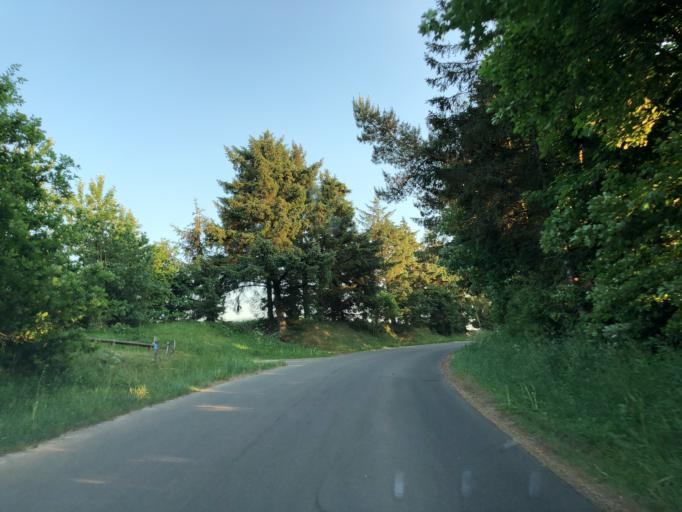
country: DK
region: Central Jutland
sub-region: Struer Kommune
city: Struer
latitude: 56.4300
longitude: 8.5054
